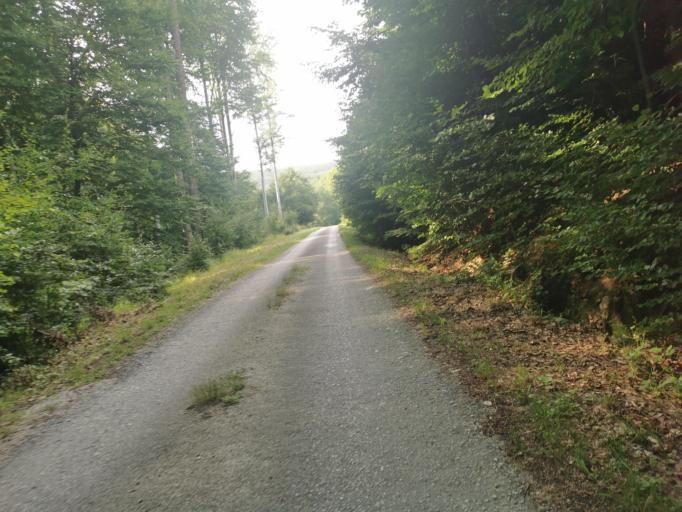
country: SK
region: Nitriansky
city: Stara Tura
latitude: 48.8272
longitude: 17.6289
